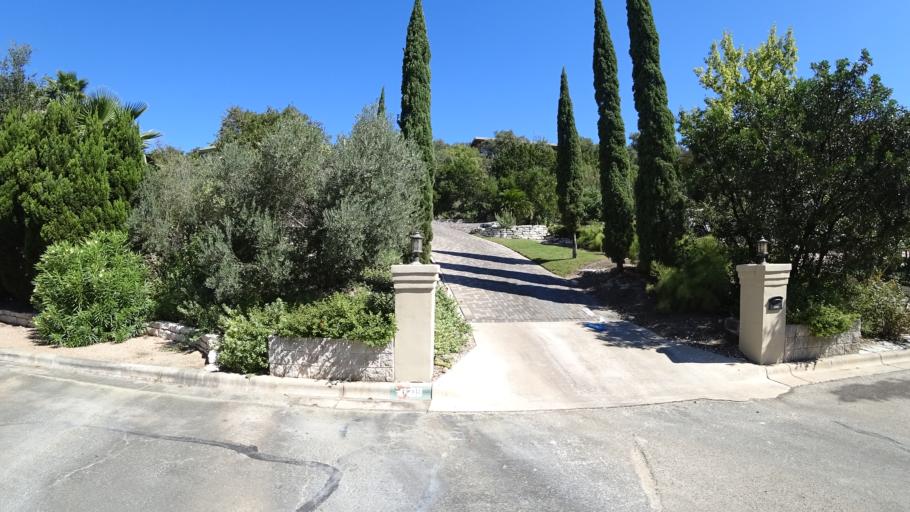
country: US
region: Texas
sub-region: Travis County
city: West Lake Hills
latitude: 30.3222
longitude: -97.7720
